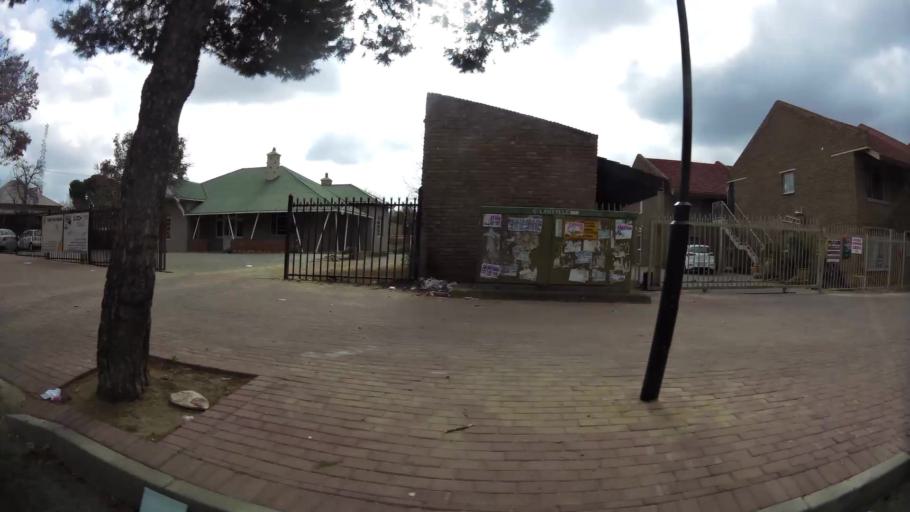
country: ZA
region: Orange Free State
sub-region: Mangaung Metropolitan Municipality
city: Bloemfontein
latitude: -29.1235
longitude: 26.2096
